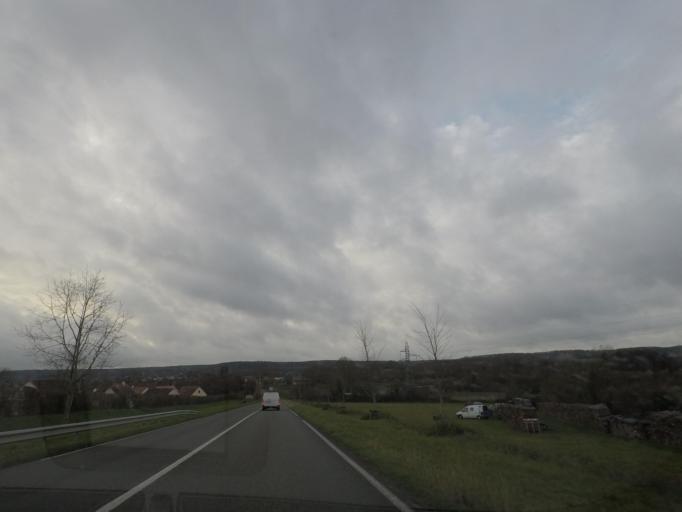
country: FR
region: Pays de la Loire
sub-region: Departement de la Sarthe
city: Vibraye
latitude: 48.0691
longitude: 0.7290
